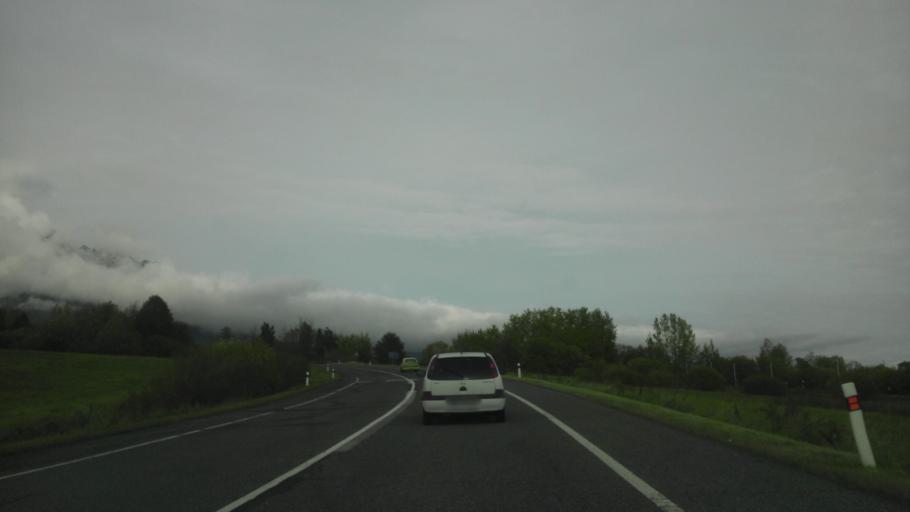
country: SK
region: Presovsky
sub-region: Okres Poprad
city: Nova Lesna
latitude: 49.1116
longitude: 20.2640
